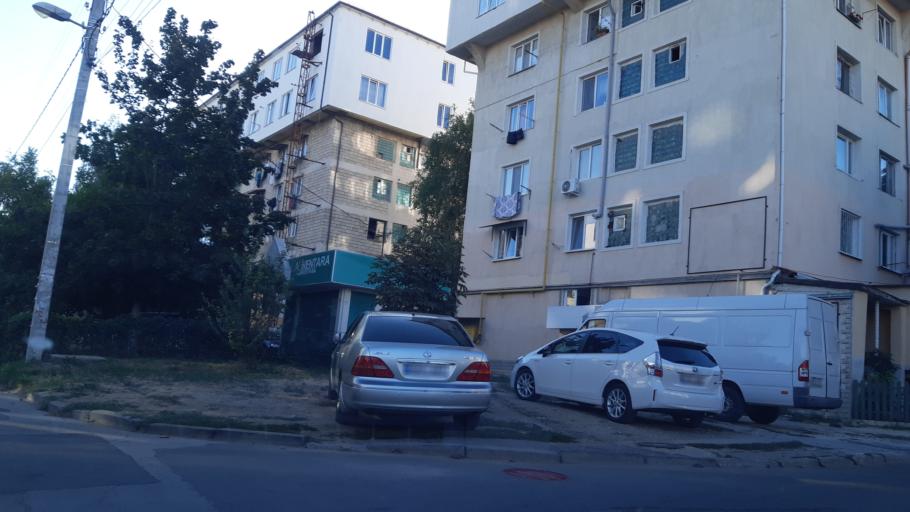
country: MD
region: Chisinau
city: Vatra
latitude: 47.0329
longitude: 28.7781
